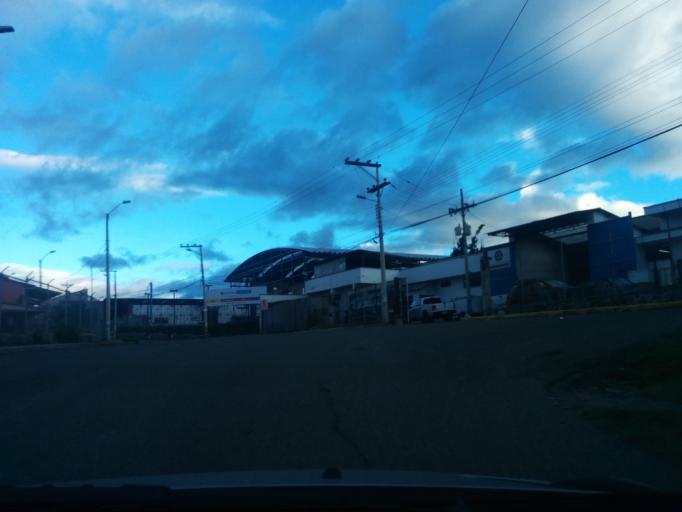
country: EC
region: Azuay
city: Cuenca
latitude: -2.8833
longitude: -78.9713
